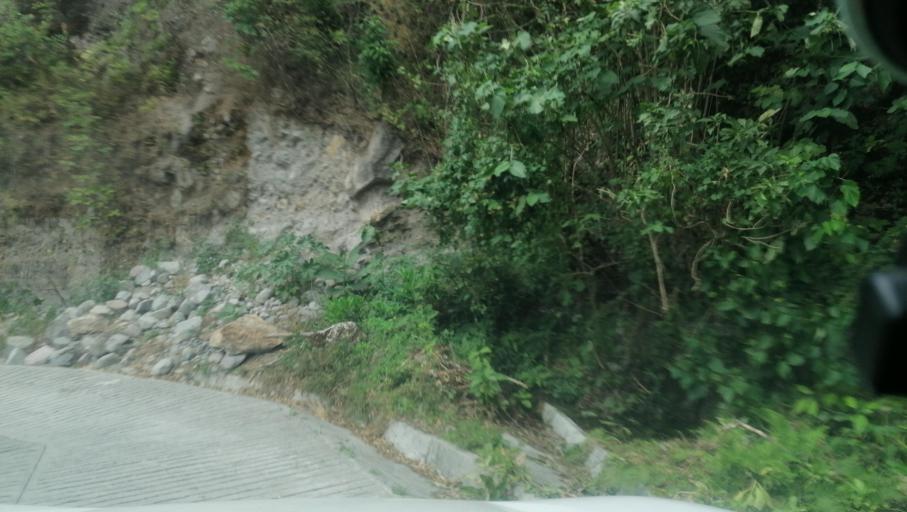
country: MX
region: Chiapas
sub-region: Cacahoatan
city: Benito Juarez
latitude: 15.1641
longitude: -92.1781
